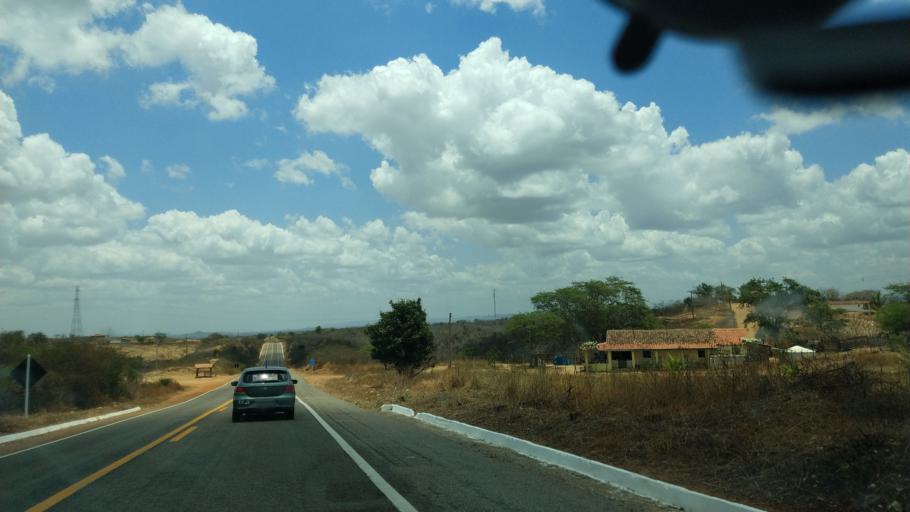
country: BR
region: Rio Grande do Norte
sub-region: Cerro Cora
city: Cerro Cora
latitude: -6.1879
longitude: -36.2393
